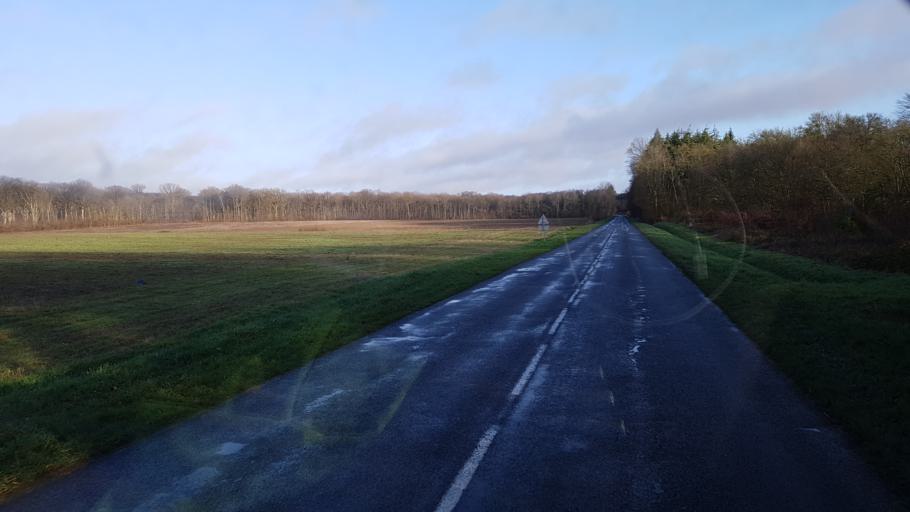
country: FR
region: Centre
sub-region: Departement du Loiret
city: Chilleurs-aux-Bois
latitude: 48.0075
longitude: 2.1974
